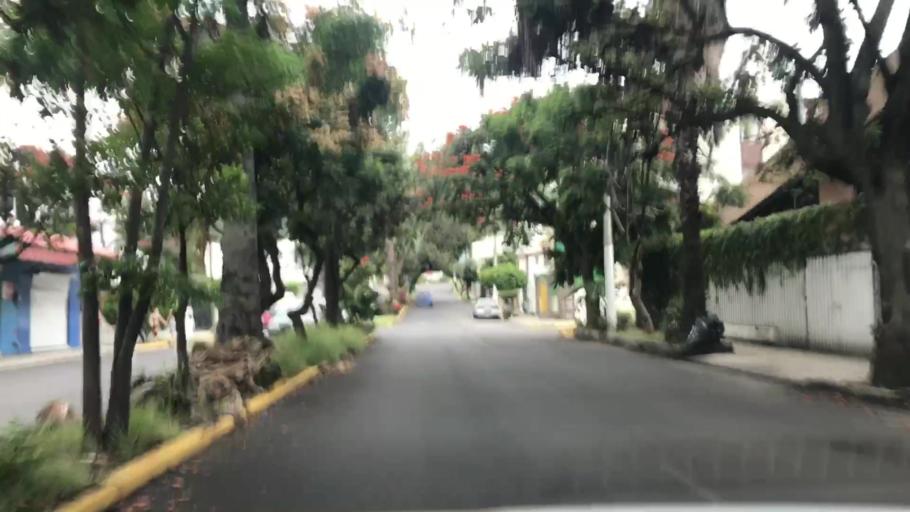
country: MX
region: Jalisco
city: Guadalajara
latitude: 20.6232
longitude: -103.4093
